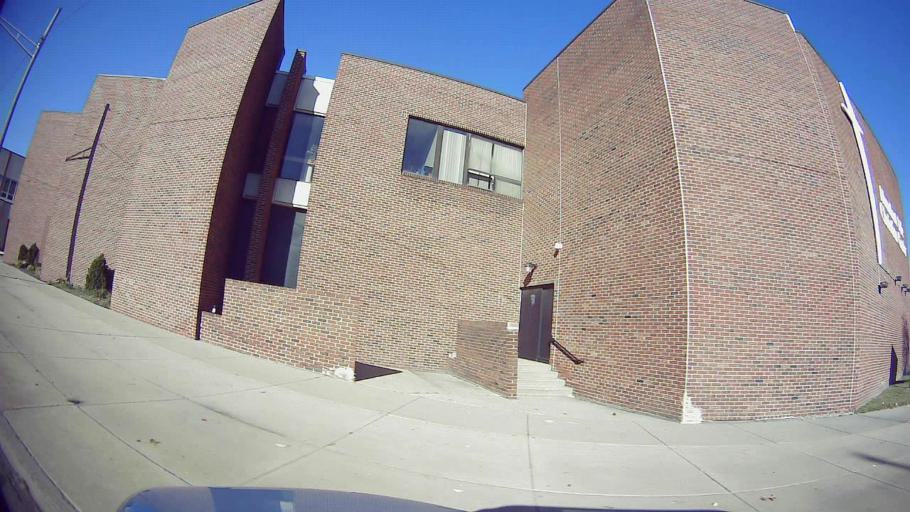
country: US
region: Michigan
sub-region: Wayne County
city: Redford
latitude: 42.4295
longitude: -83.2894
